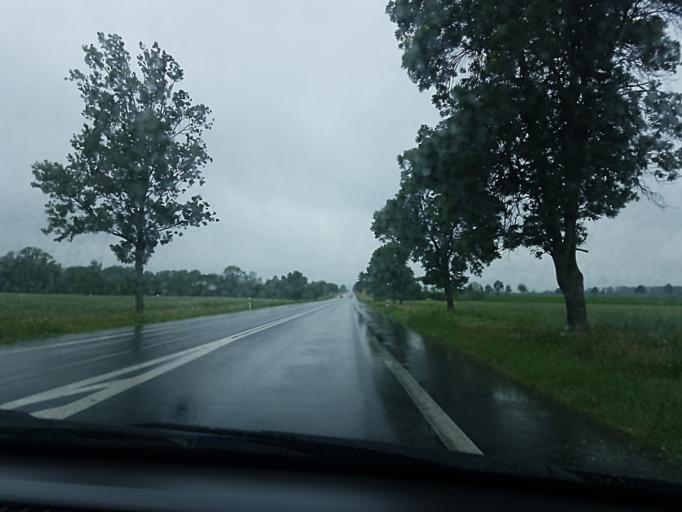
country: PL
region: Greater Poland Voivodeship
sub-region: Powiat kolski
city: Chodow
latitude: 52.2497
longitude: 19.0216
